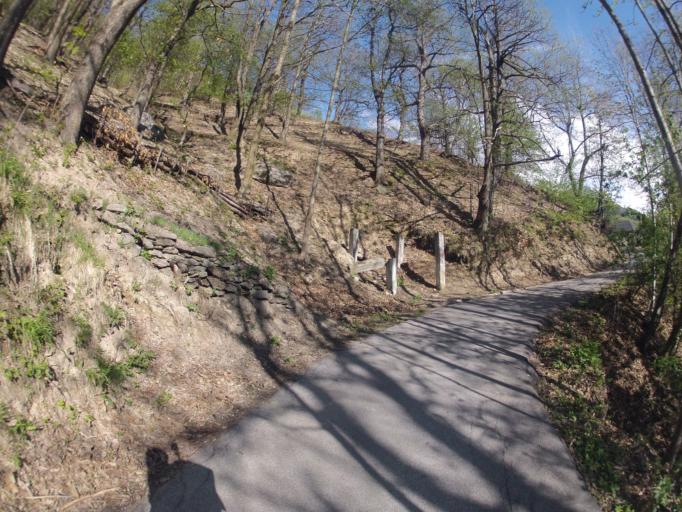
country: IT
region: Piedmont
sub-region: Provincia di Cuneo
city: Vernante
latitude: 44.2827
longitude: 7.5688
